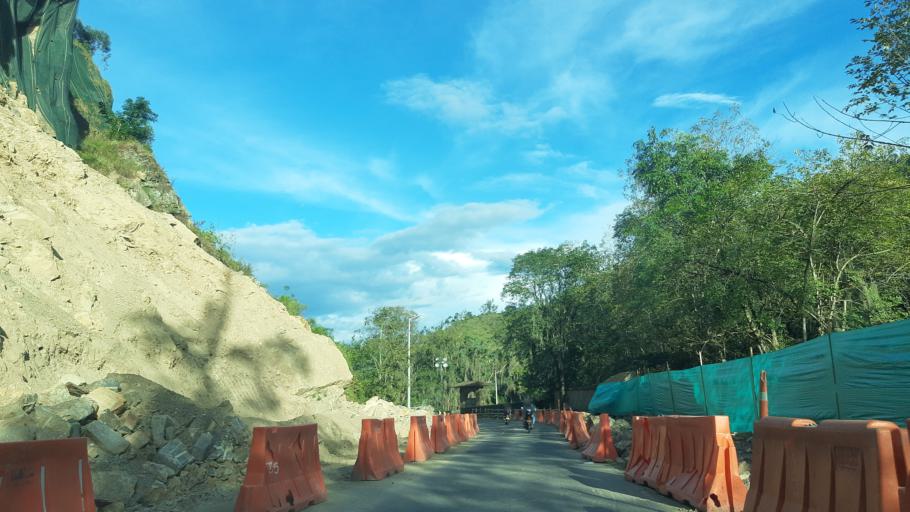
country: CO
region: Cundinamarca
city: Macheta
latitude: 5.0750
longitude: -73.5828
